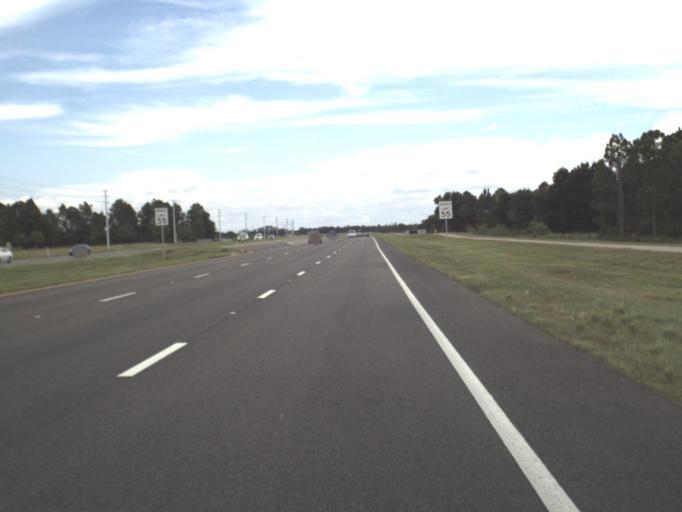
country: US
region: Florida
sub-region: Hillsborough County
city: Pebble Creek
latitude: 28.1888
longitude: -82.3437
